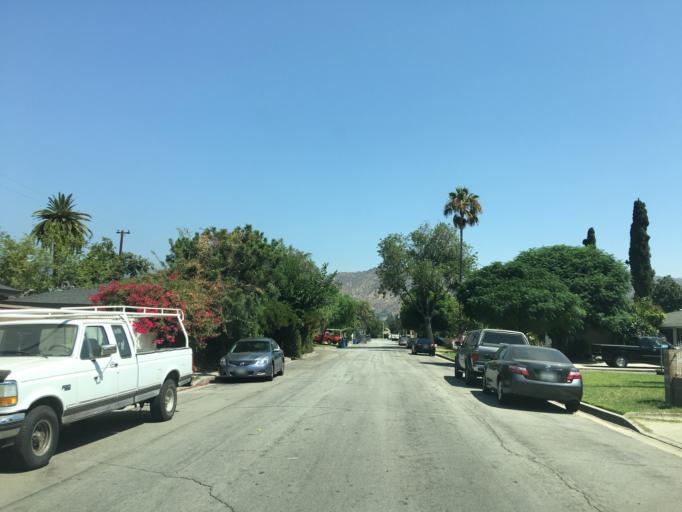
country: US
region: California
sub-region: Los Angeles County
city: Citrus
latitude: 34.1238
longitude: -117.8887
